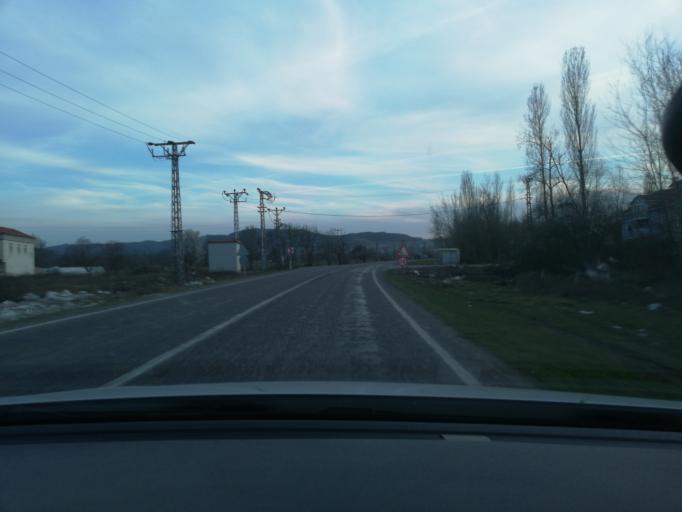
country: TR
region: Zonguldak
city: Saltukova
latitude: 41.5137
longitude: 32.1033
